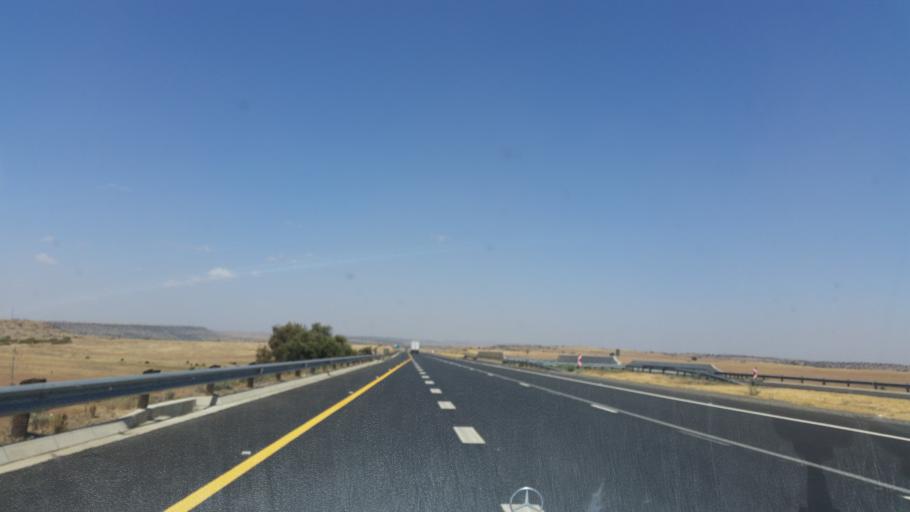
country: ZA
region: Orange Free State
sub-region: Lejweleputswa District Municipality
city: Winburg
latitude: -28.5052
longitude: 26.9950
